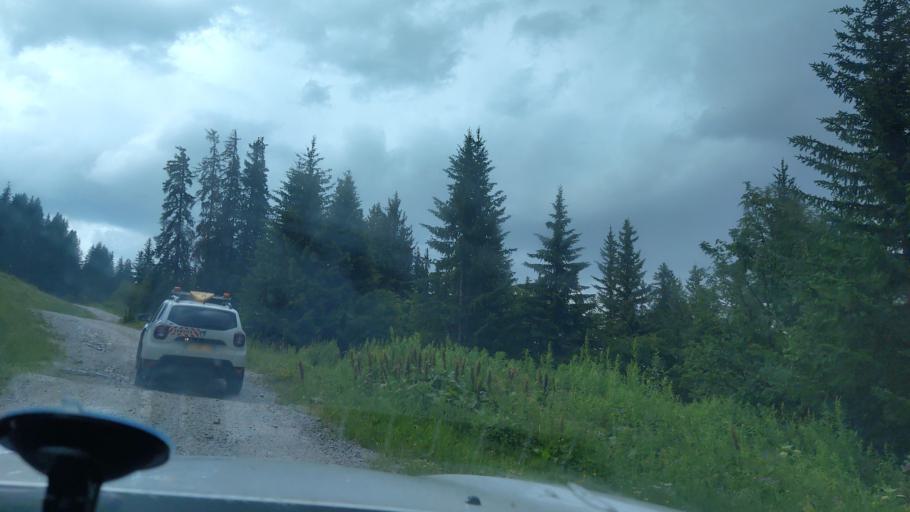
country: FR
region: Rhone-Alpes
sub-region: Departement de la Savoie
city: Courchevel
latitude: 45.3949
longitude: 6.6415
